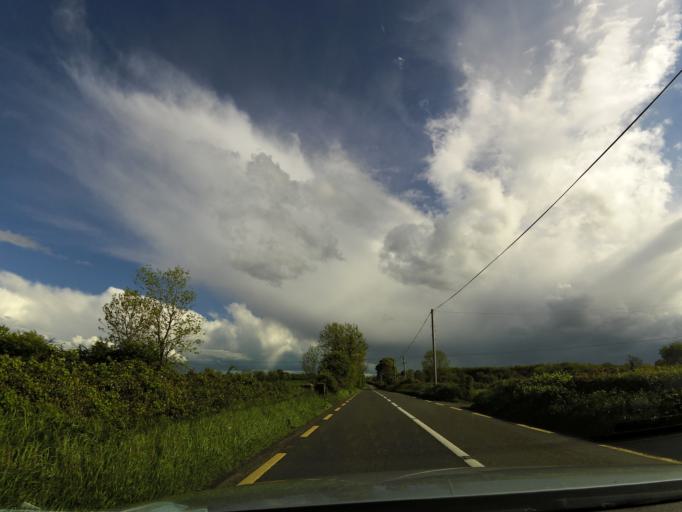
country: IE
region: Munster
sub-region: North Tipperary
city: Templemore
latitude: 52.7827
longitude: -7.8428
